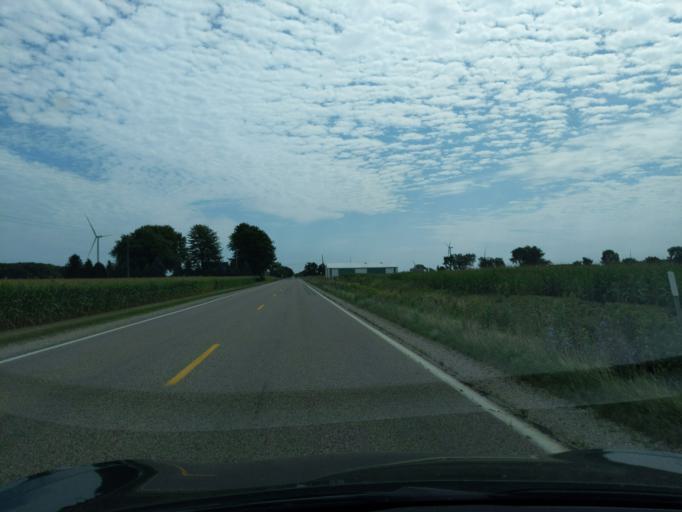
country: US
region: Michigan
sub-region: Gratiot County
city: Ithaca
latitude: 43.2917
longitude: -84.5132
